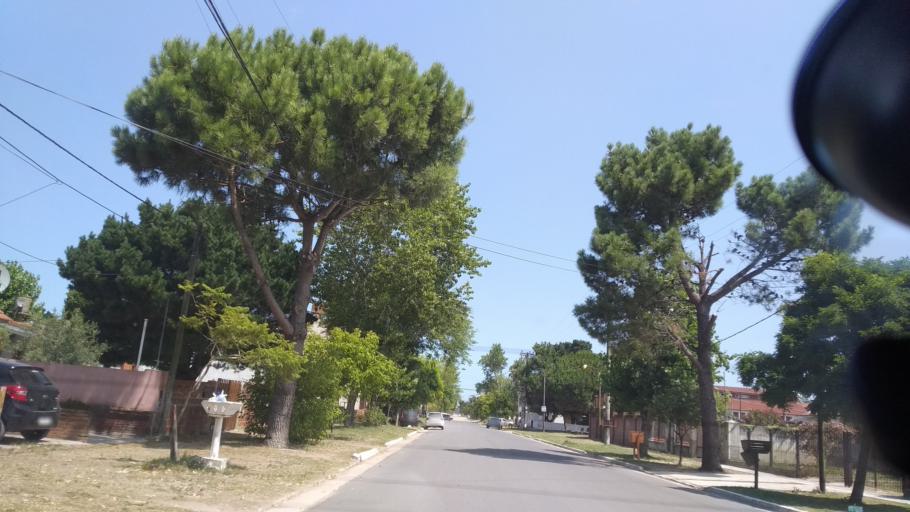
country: AR
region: Buenos Aires
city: Mar del Tuyu
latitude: -36.5796
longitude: -56.6936
